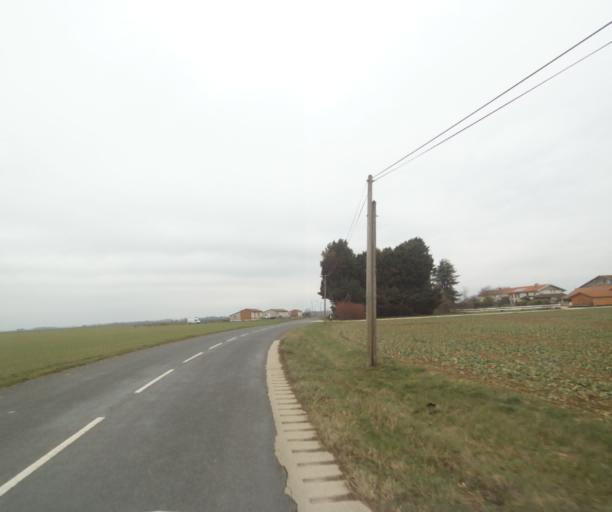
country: FR
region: Champagne-Ardenne
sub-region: Departement de la Haute-Marne
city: Villiers-en-Lieu
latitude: 48.6458
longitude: 4.7630
